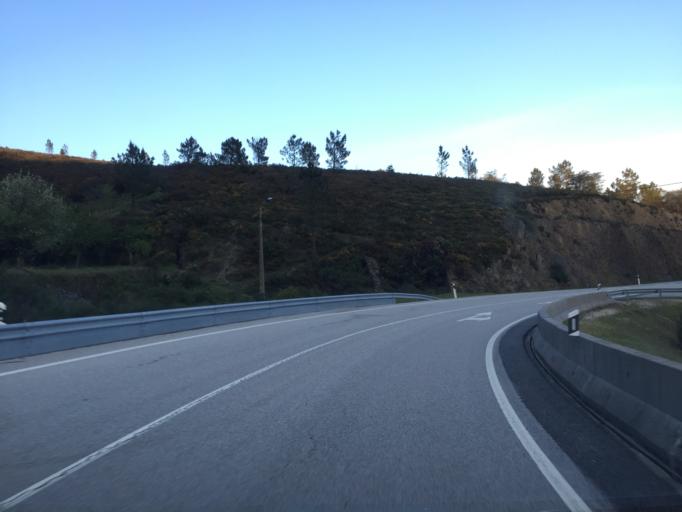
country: PT
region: Coimbra
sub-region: Pampilhosa da Serra
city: Pampilhosa da Serra
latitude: 40.1092
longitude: -8.0096
